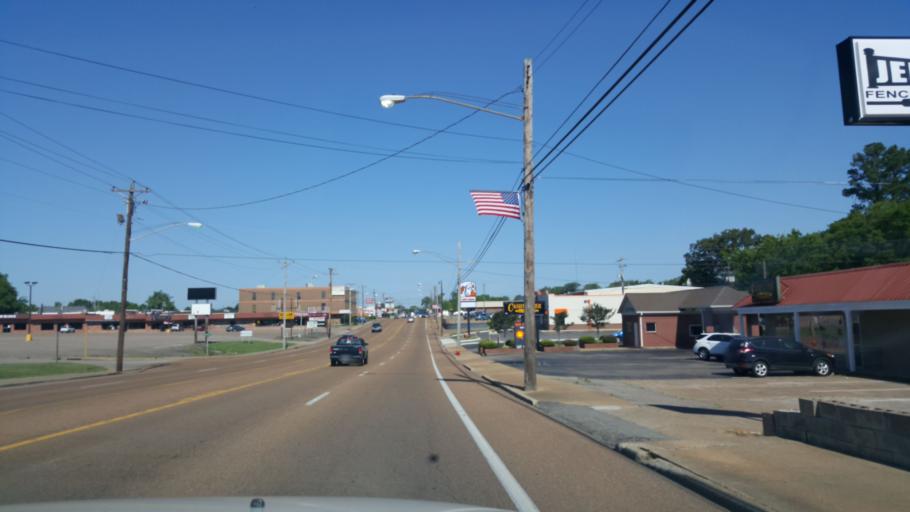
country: US
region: Tennessee
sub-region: Hardin County
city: Savannah
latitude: 35.2267
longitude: -88.2267
